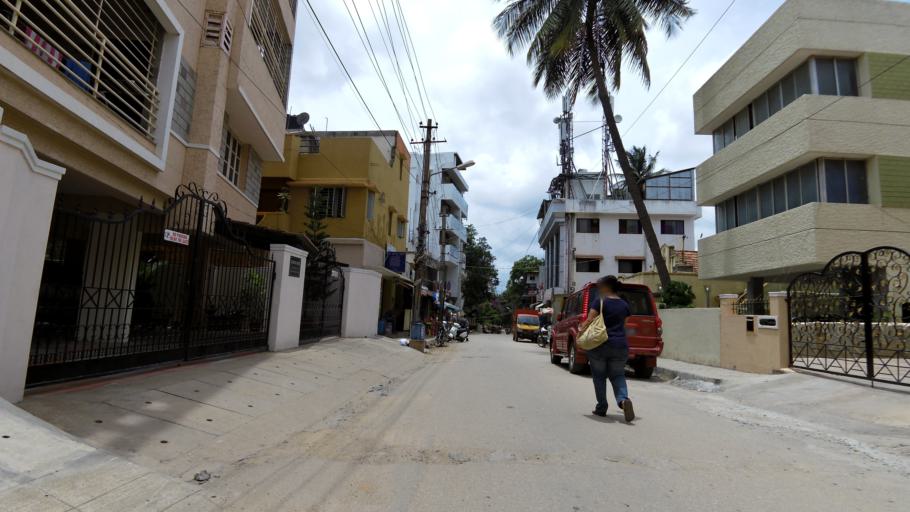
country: IN
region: Karnataka
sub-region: Bangalore Urban
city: Bangalore
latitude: 13.0042
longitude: 77.6230
